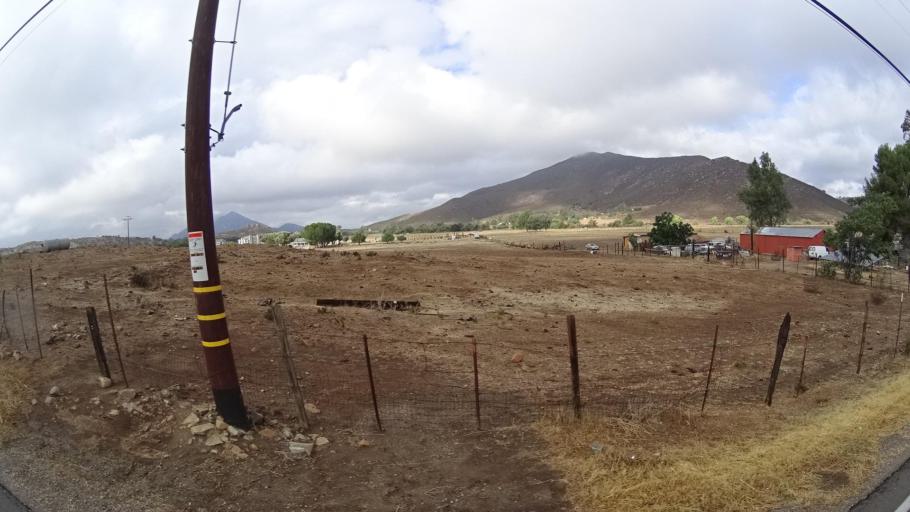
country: MX
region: Baja California
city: Tecate
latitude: 32.6137
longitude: -116.6133
